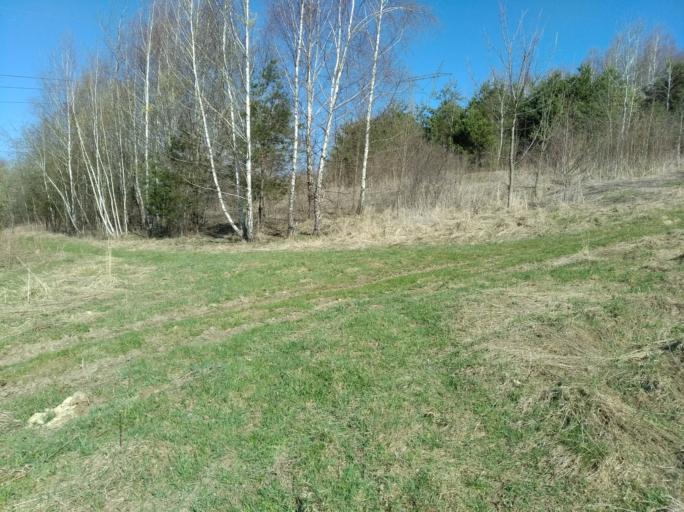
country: PL
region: Subcarpathian Voivodeship
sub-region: Powiat strzyzowski
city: Jawornik
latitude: 49.8358
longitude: 21.8503
